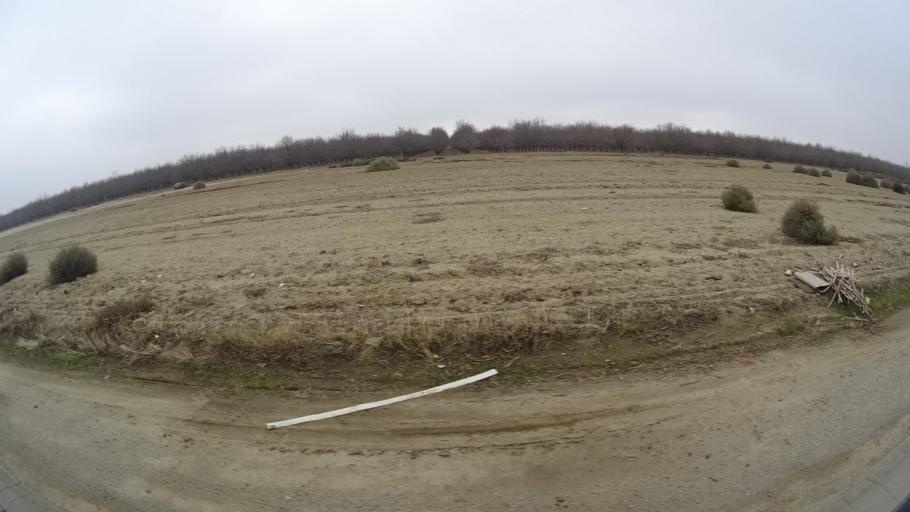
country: US
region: California
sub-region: Kern County
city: Greenfield
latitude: 35.0946
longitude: -119.1070
